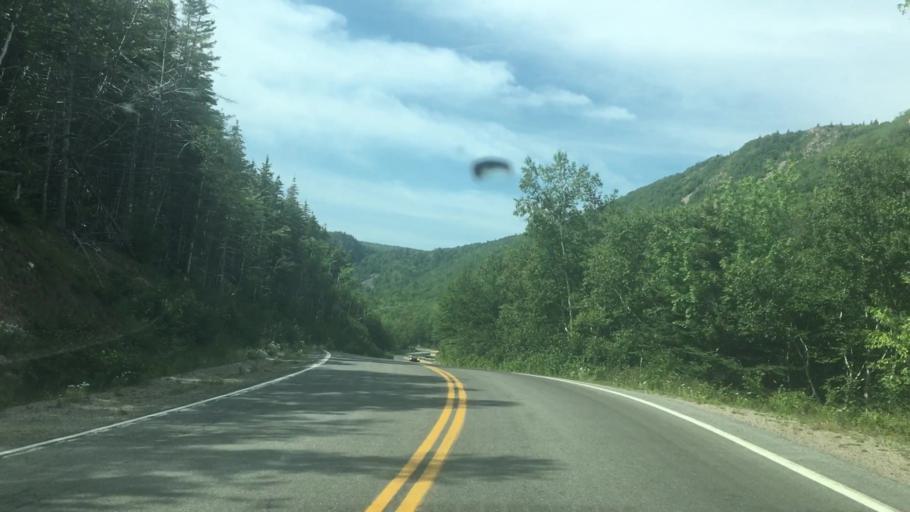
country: CA
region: Nova Scotia
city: Sydney Mines
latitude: 46.5820
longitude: -60.3930
